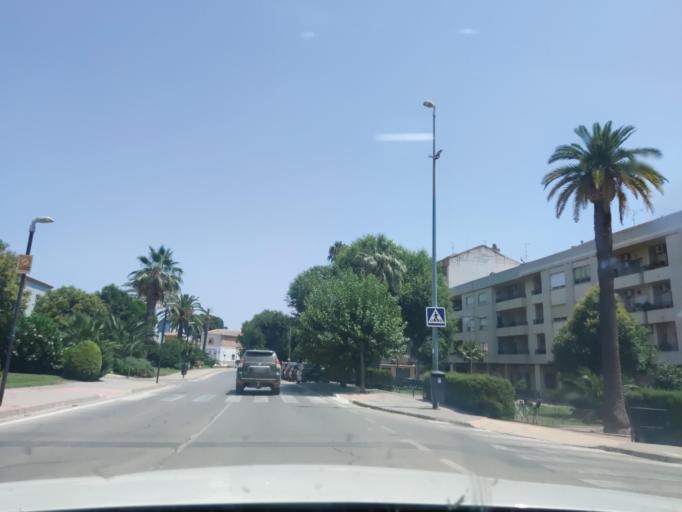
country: ES
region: Castille-La Mancha
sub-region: Provincia de Albacete
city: Hellin
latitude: 38.5101
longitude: -1.6938
